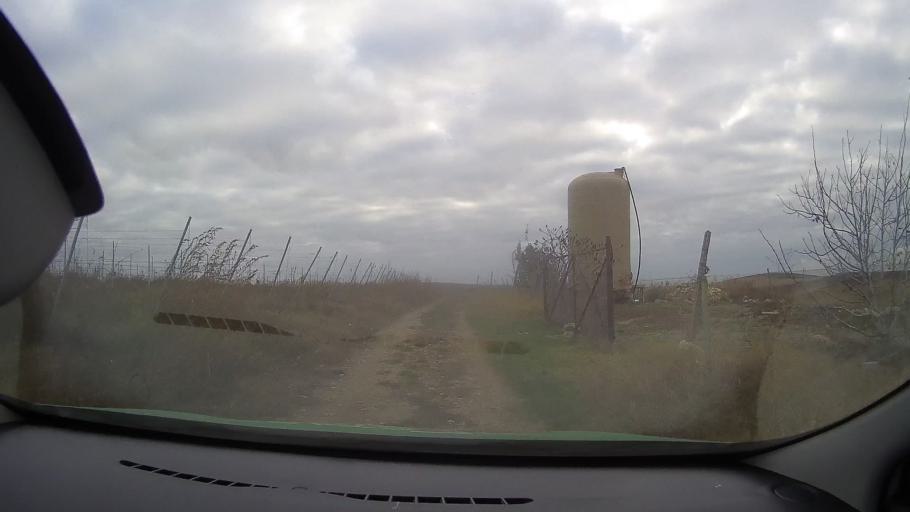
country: RO
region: Tulcea
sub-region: Comuna Jurilovca
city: Jurilovca
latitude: 44.7680
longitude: 28.9175
